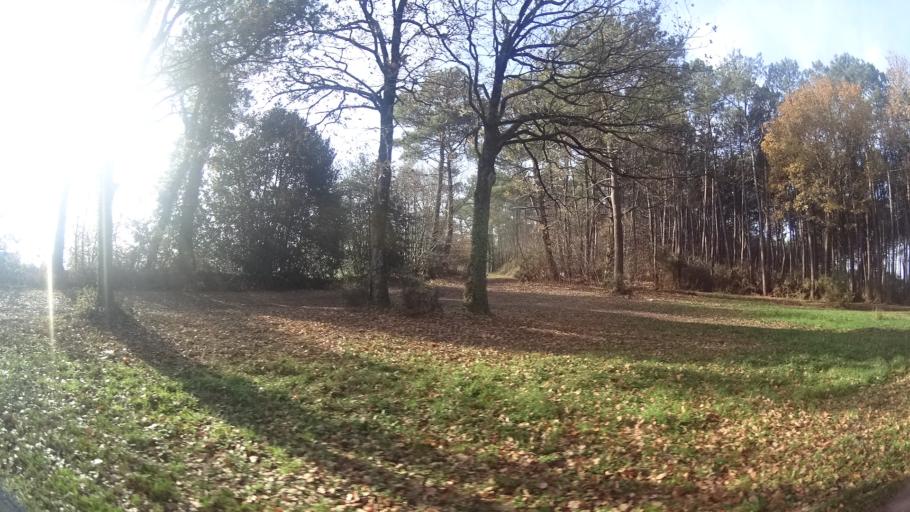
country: FR
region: Brittany
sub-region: Departement du Morbihan
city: Allaire
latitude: 47.6028
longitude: -2.1478
